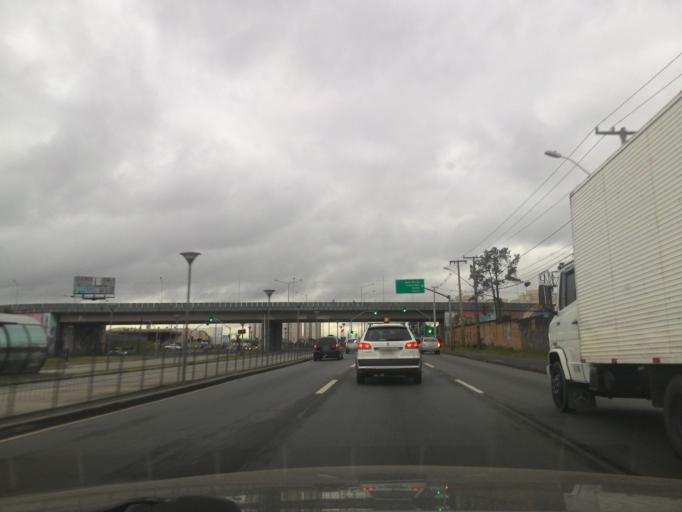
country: BR
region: Parana
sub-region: Curitiba
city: Curitiba
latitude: -25.4969
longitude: -49.2761
